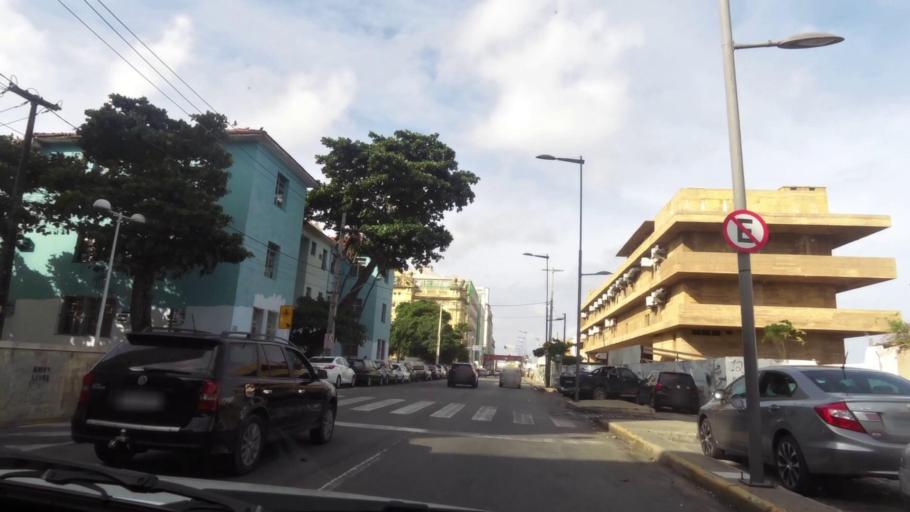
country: BR
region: Pernambuco
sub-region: Recife
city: Recife
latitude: -8.0593
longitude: -34.8701
